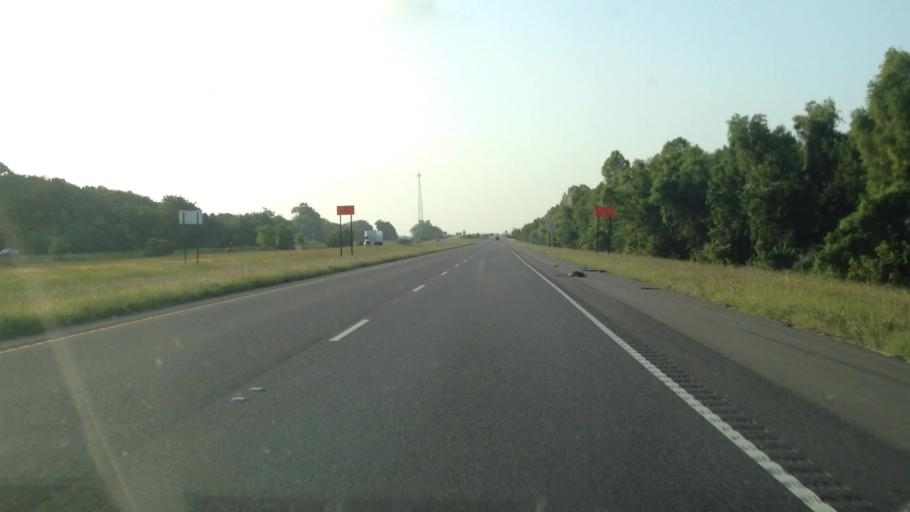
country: US
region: Louisiana
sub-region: Rapides Parish
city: Boyce
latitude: 31.3981
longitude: -92.7010
